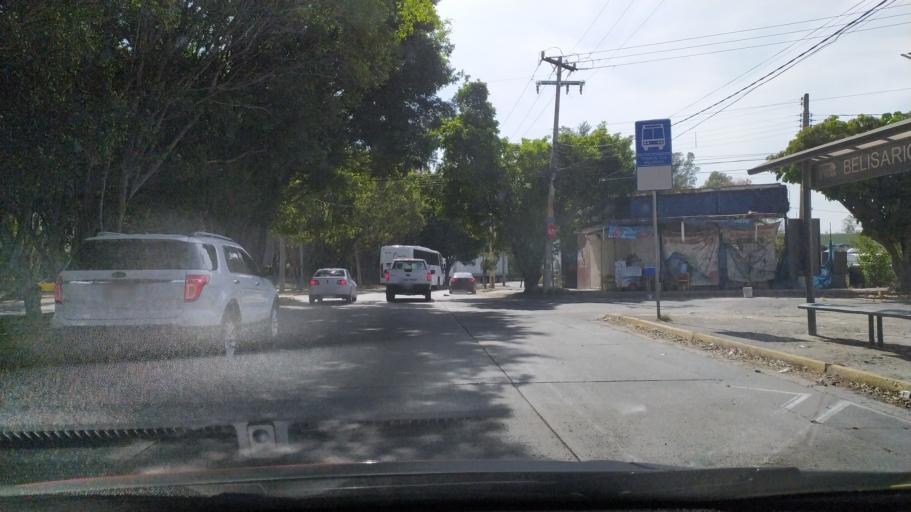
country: MX
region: Jalisco
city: Tlaquepaque
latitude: 20.6507
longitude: -103.3374
